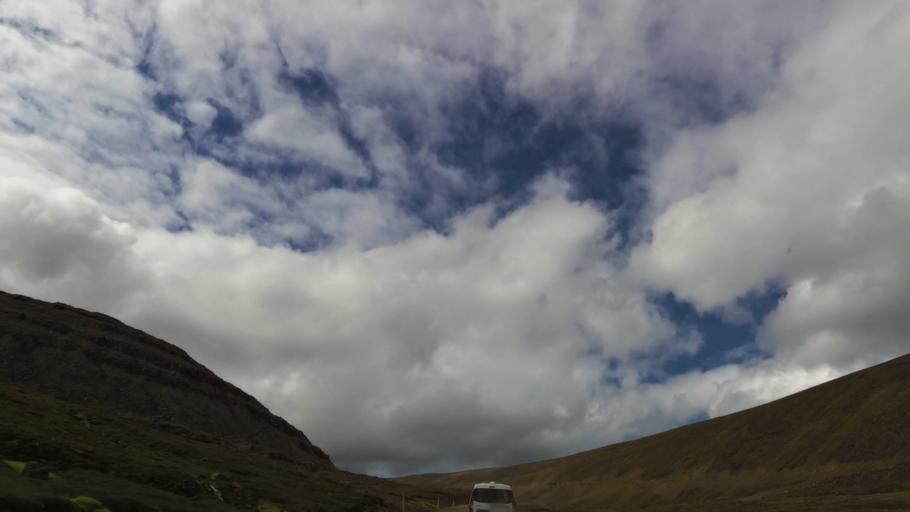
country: IS
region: Westfjords
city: Isafjoerdur
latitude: 66.1699
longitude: -23.3496
